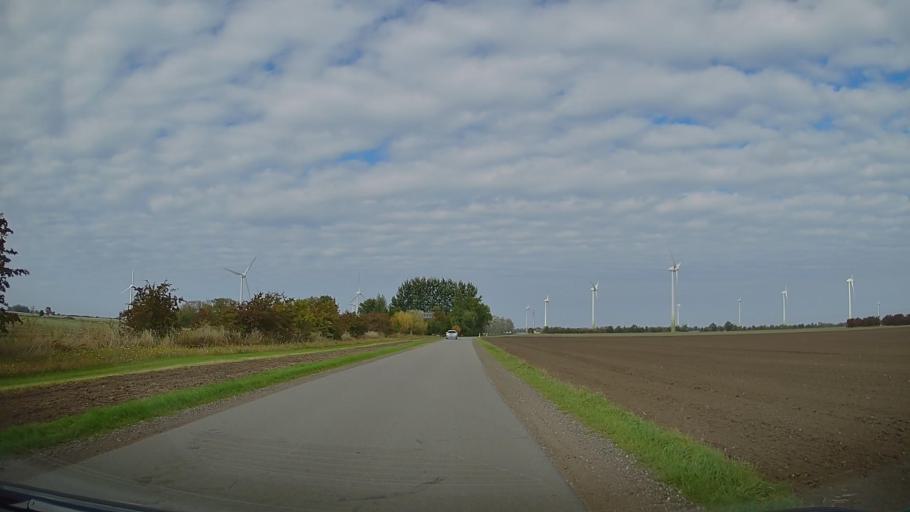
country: DE
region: Schleswig-Holstein
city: Grossenbrode
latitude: 54.5010
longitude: 11.0594
